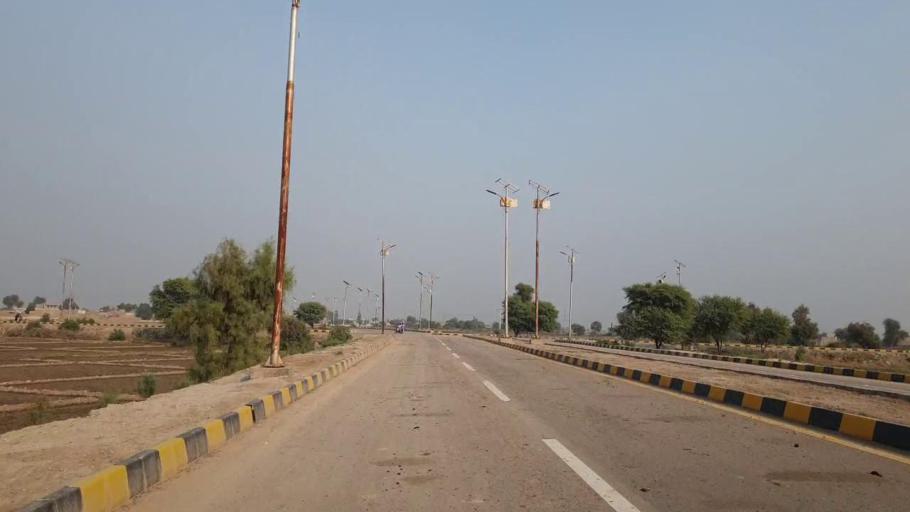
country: PK
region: Sindh
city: Bhan
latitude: 26.4755
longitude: 67.7237
